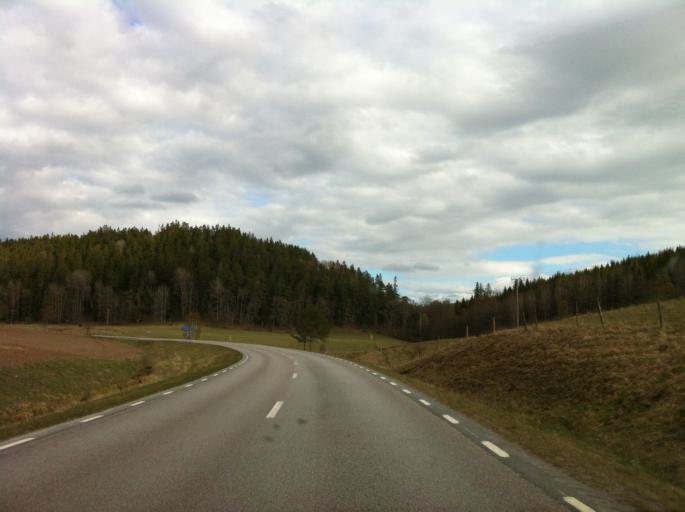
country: SE
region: OEstergoetland
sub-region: Kinda Kommun
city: Rimforsa
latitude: 58.0478
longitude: 15.8462
